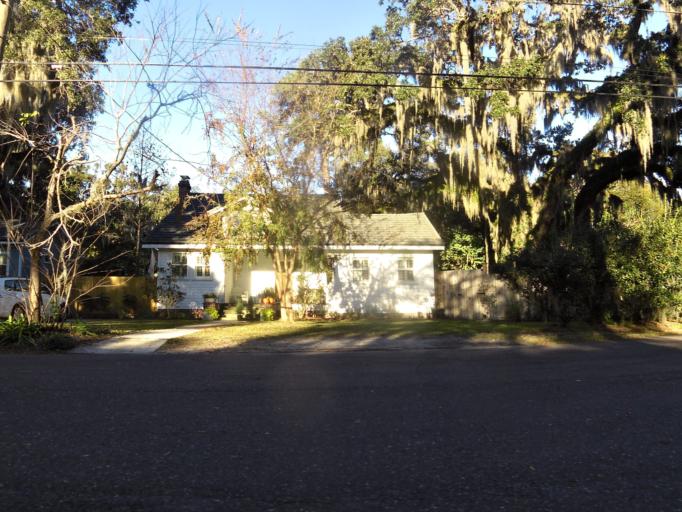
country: US
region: Florida
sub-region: Duval County
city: Jacksonville
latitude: 30.2763
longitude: -81.7028
